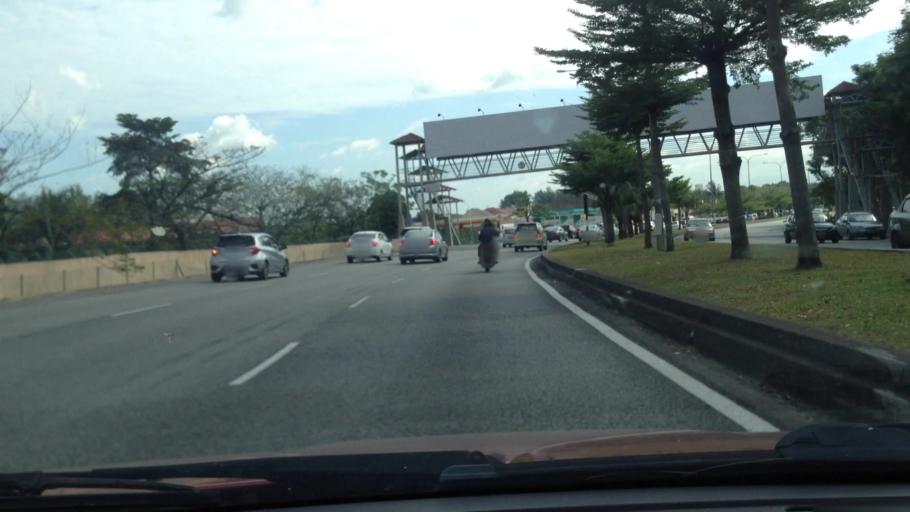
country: MY
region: Selangor
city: Subang Jaya
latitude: 3.0547
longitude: 101.5765
